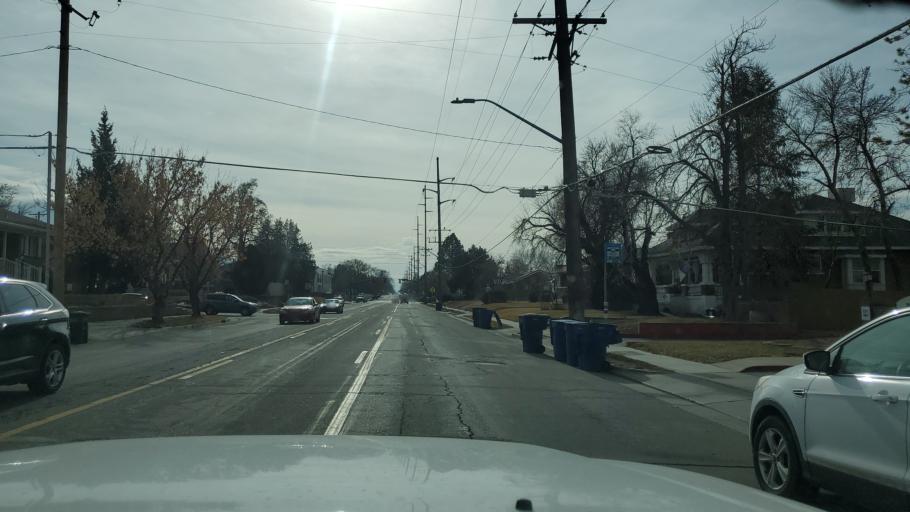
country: US
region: Utah
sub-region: Salt Lake County
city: South Salt Lake
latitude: 40.7146
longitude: -111.8653
